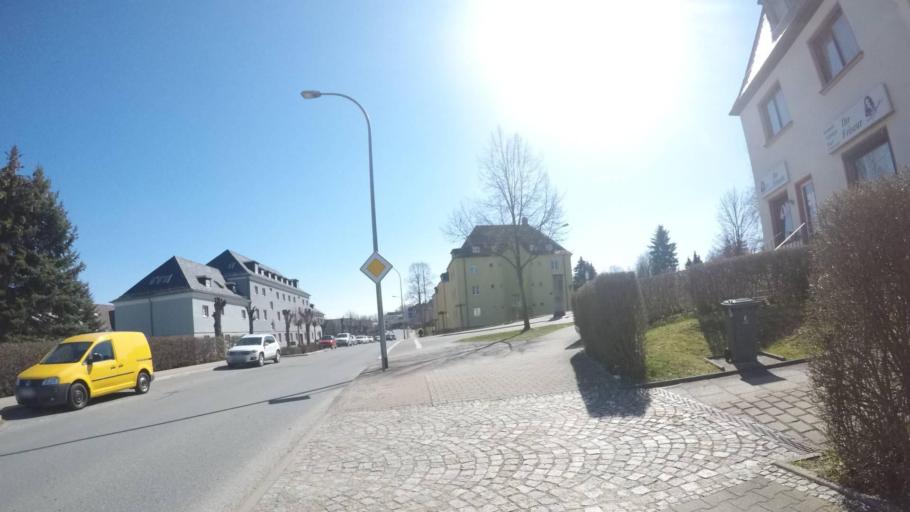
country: DE
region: Saxony
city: Limbach-Oberfrohna
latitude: 50.8643
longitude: 12.7544
